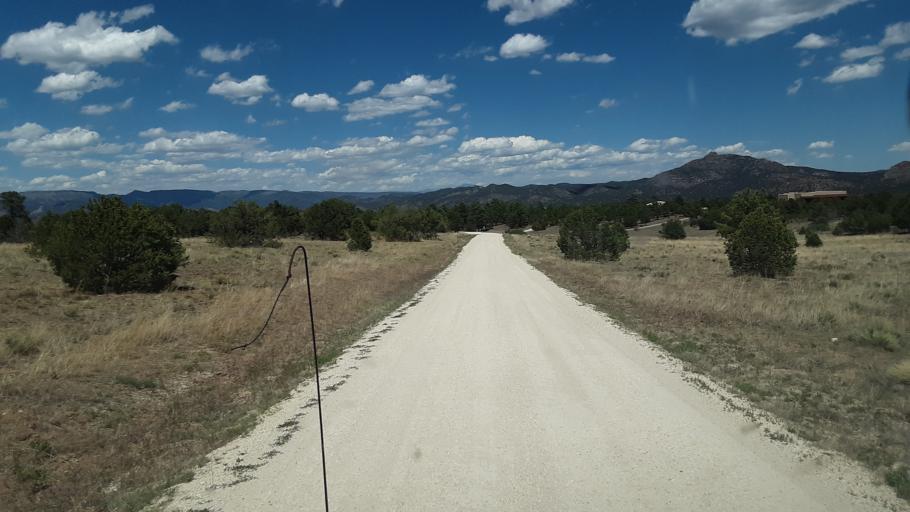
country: US
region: Colorado
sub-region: Custer County
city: Westcliffe
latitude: 38.3168
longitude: -105.6265
